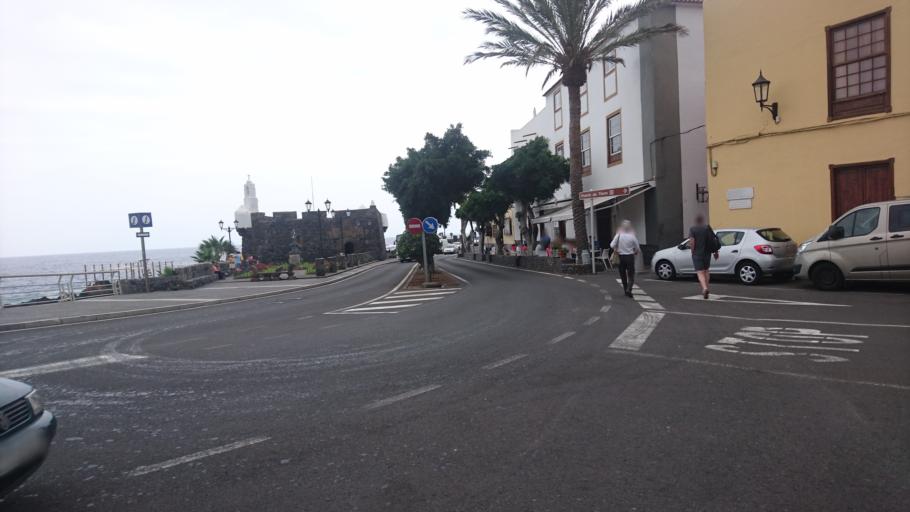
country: ES
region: Canary Islands
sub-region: Provincia de Santa Cruz de Tenerife
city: Garachico
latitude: 28.3725
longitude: -16.7659
